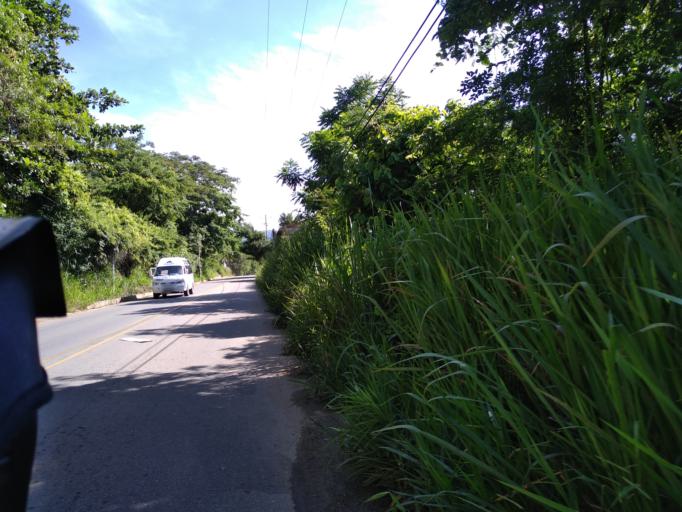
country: CO
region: Santander
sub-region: San Gil
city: San Gil
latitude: 6.5266
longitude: -73.1252
